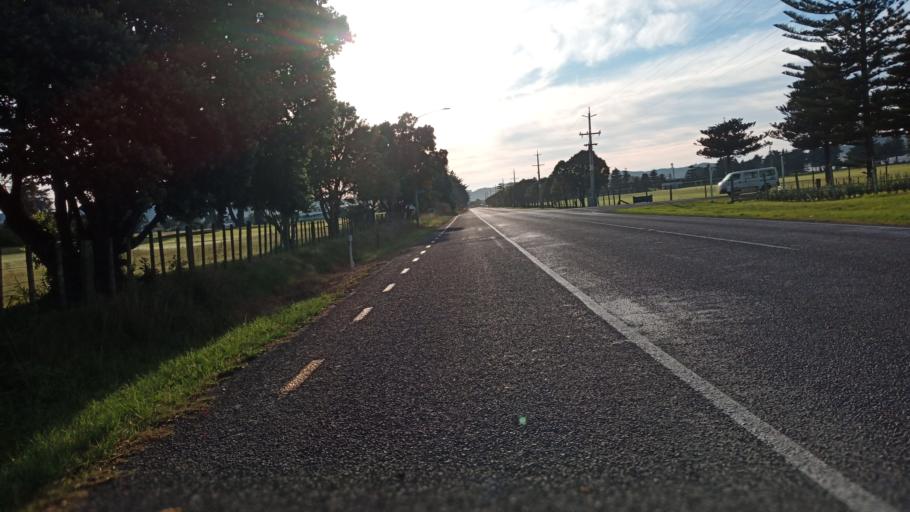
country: NZ
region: Gisborne
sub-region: Gisborne District
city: Gisborne
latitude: -38.6714
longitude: 177.9915
